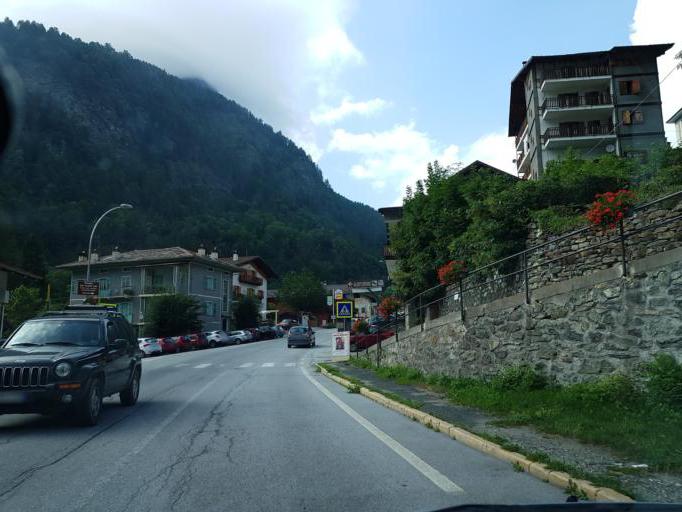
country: IT
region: Piedmont
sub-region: Provincia di Cuneo
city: Casteldelfino
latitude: 44.5895
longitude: 7.0694
